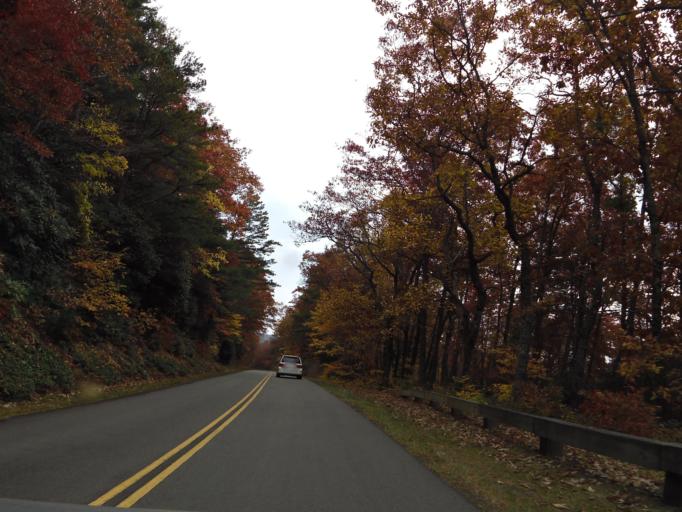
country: US
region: North Carolina
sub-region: Ashe County
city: Jefferson
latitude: 36.3202
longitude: -81.3700
